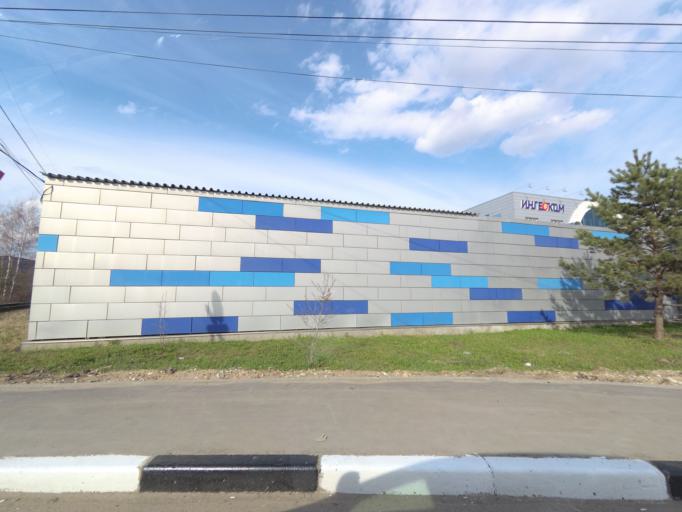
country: RU
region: Moskovskaya
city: Lobnya
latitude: 56.0101
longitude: 37.4375
